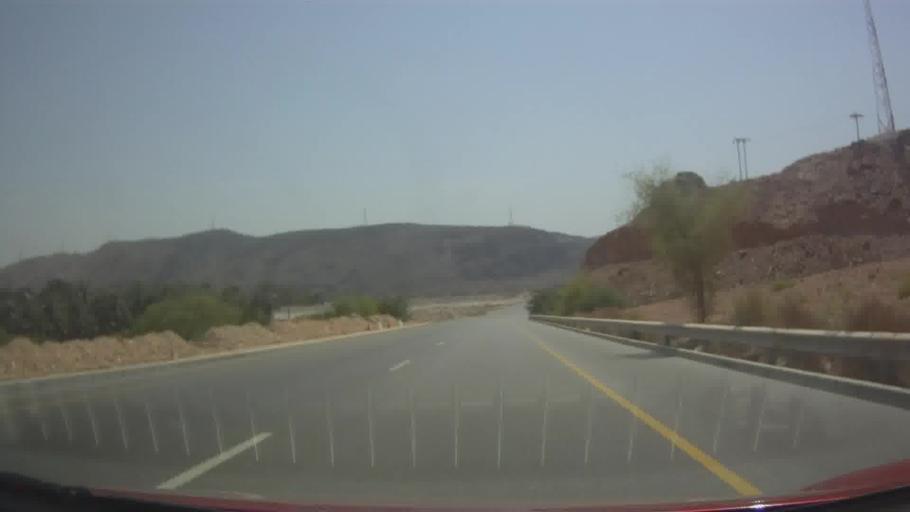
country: OM
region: Muhafazat Masqat
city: Muscat
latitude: 23.5156
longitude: 58.6338
